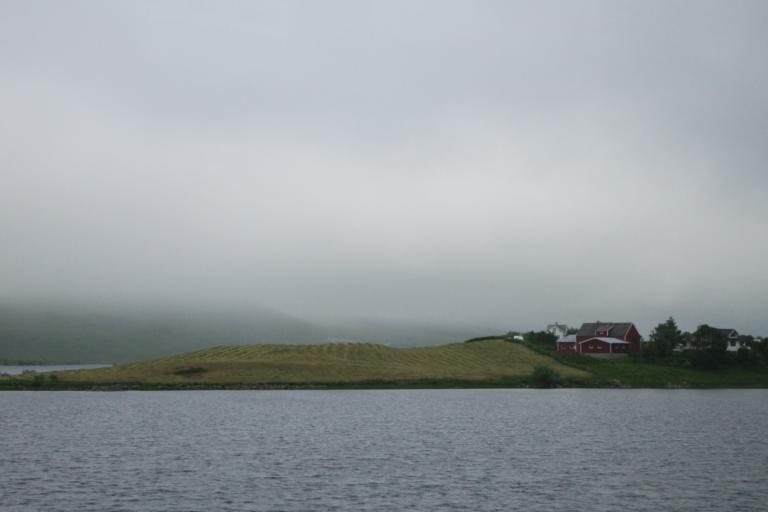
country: NO
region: Nordland
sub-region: Vestvagoy
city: Leknes
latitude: 68.1854
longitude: 13.6430
